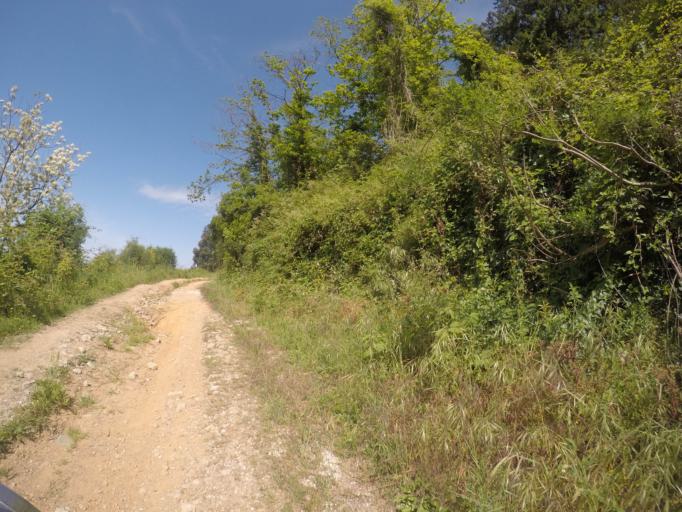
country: IT
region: Tuscany
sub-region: Provincia di Massa-Carrara
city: Massa
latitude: 44.0599
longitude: 10.1037
